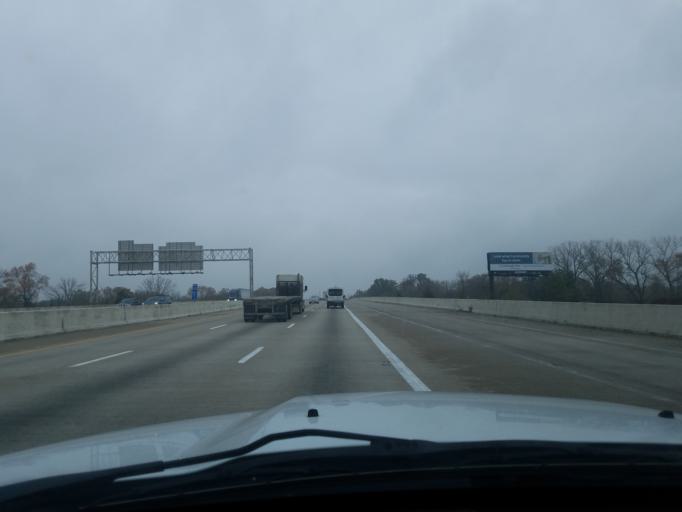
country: US
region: Indiana
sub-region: Marion County
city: Warren Park
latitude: 39.7513
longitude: -86.0334
